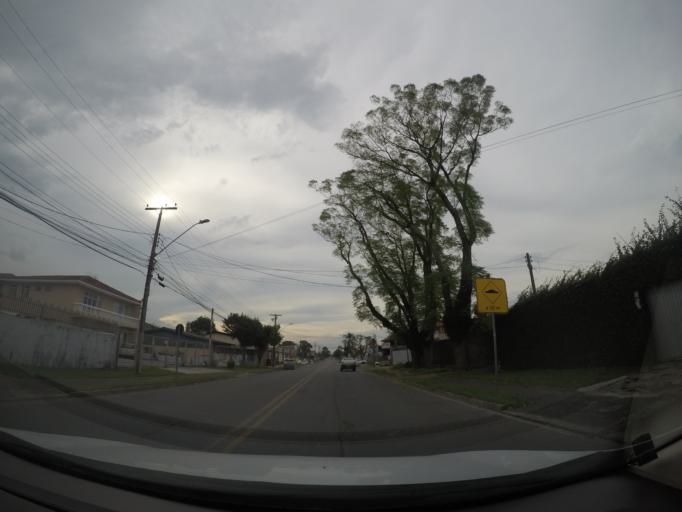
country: BR
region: Parana
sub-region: Sao Jose Dos Pinhais
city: Sao Jose dos Pinhais
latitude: -25.5074
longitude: -49.2236
